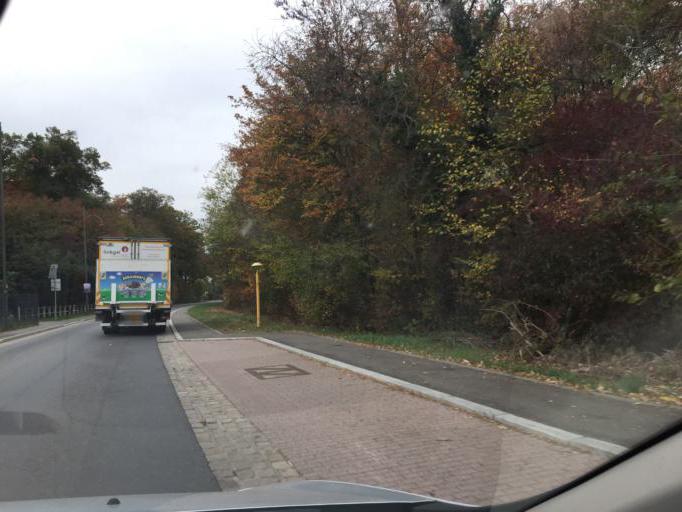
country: LU
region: Luxembourg
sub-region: Canton de Luxembourg
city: Olm
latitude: 49.6540
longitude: 5.9976
